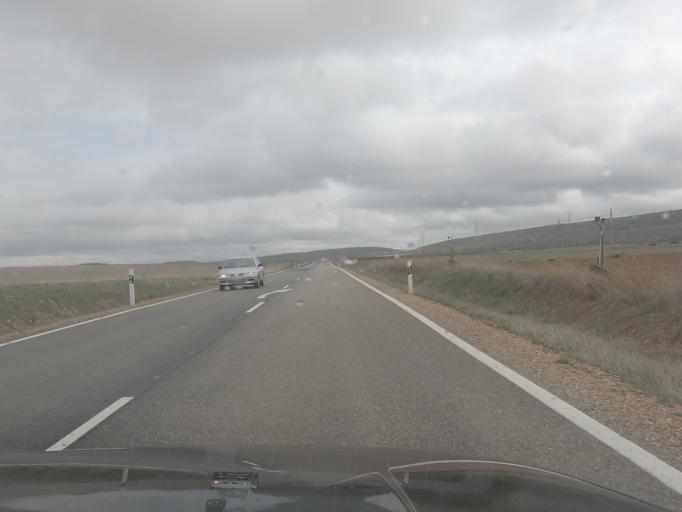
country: ES
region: Castille and Leon
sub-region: Provincia de Zamora
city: Pozuelo de Tabara
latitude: 41.7726
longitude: -5.8774
